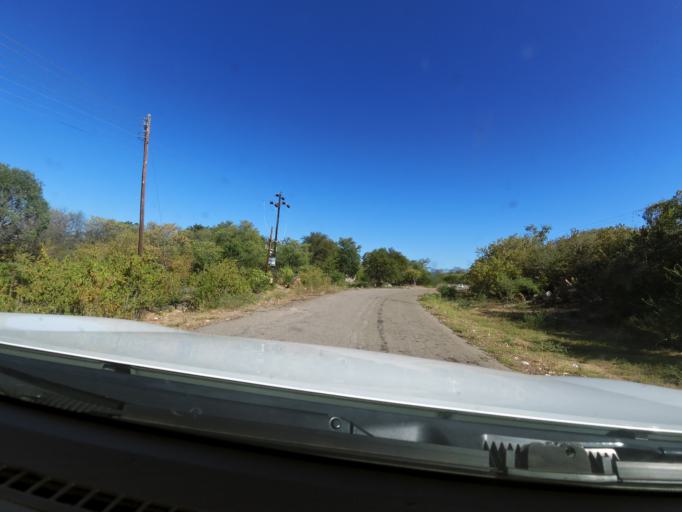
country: ZW
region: Matabeleland North
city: Kamativi Mine
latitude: -17.9431
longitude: 27.0818
